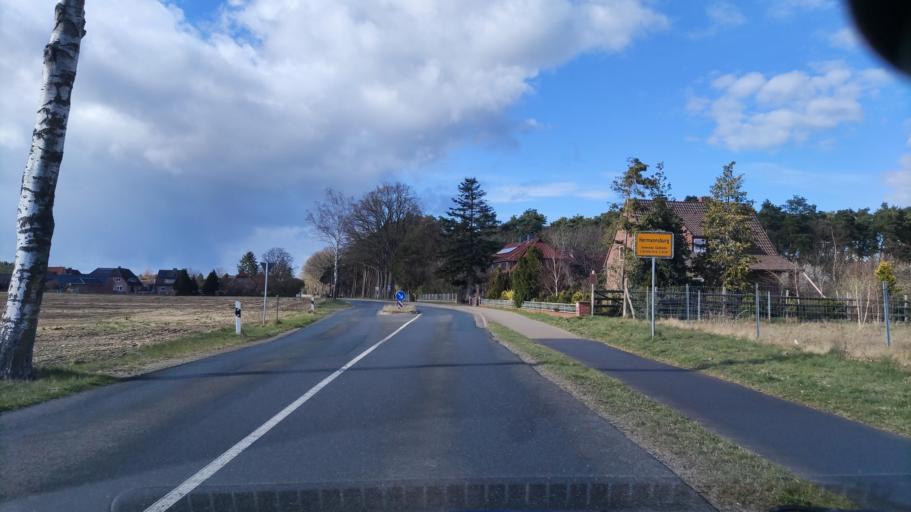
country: DE
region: Lower Saxony
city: Hermannsburg
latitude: 52.8212
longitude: 10.0948
